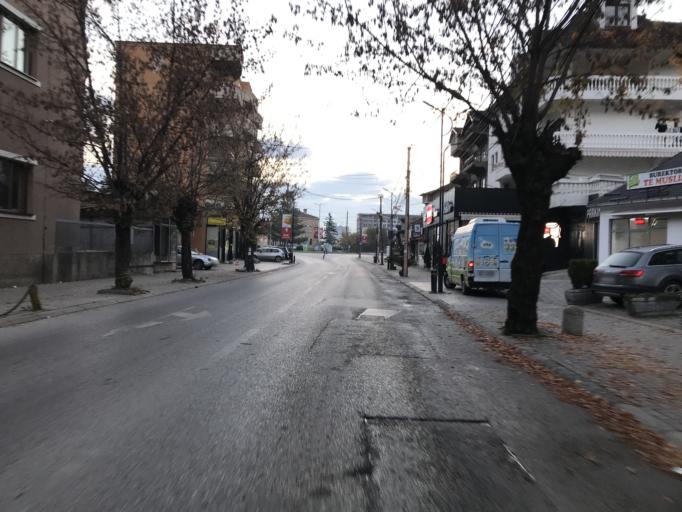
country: XK
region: Pec
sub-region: Komuna e Pejes
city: Peje
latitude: 42.6606
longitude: 20.3027
